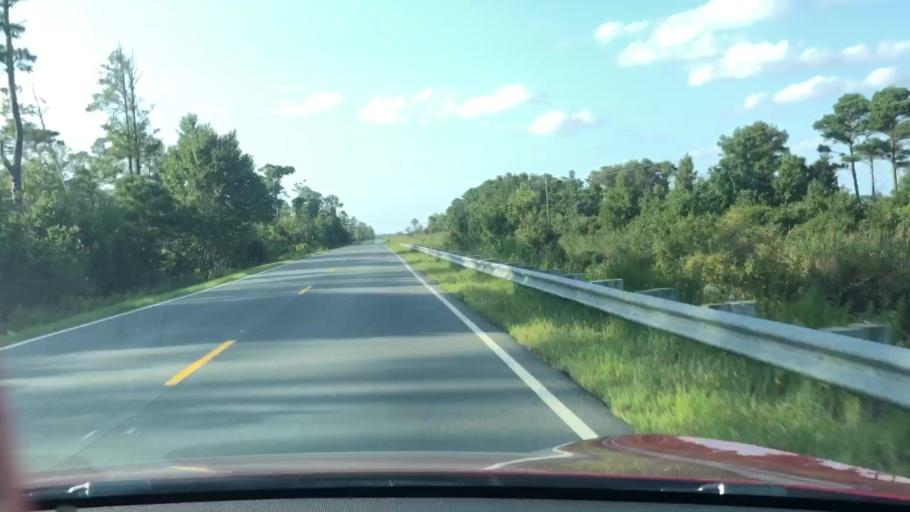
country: US
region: North Carolina
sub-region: Dare County
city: Wanchese
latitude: 35.6707
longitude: -75.7786
